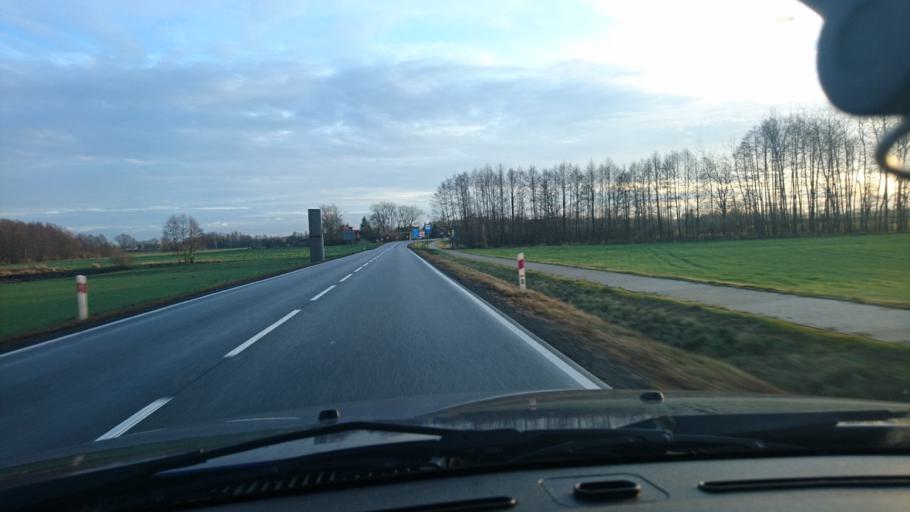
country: PL
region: Greater Poland Voivodeship
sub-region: Powiat kepinski
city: Opatow
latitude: 51.1722
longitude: 18.1458
